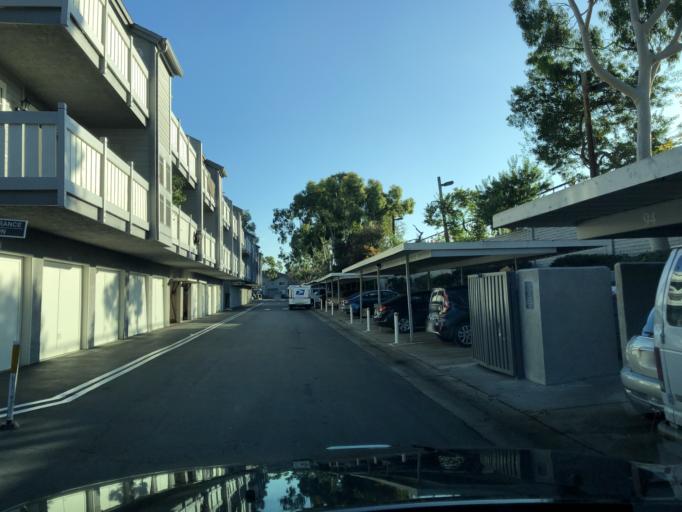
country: US
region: California
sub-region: Orange County
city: Costa Mesa
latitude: 33.6779
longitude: -117.8851
